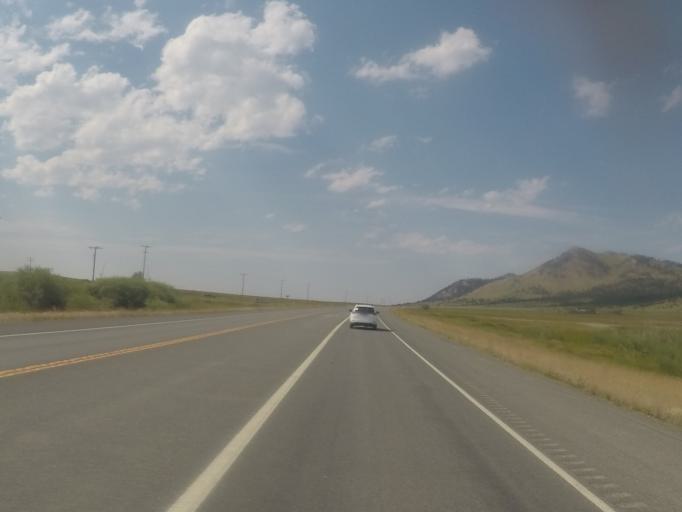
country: US
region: Montana
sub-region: Lewis and Clark County
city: East Helena
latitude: 46.5139
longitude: -111.7039
